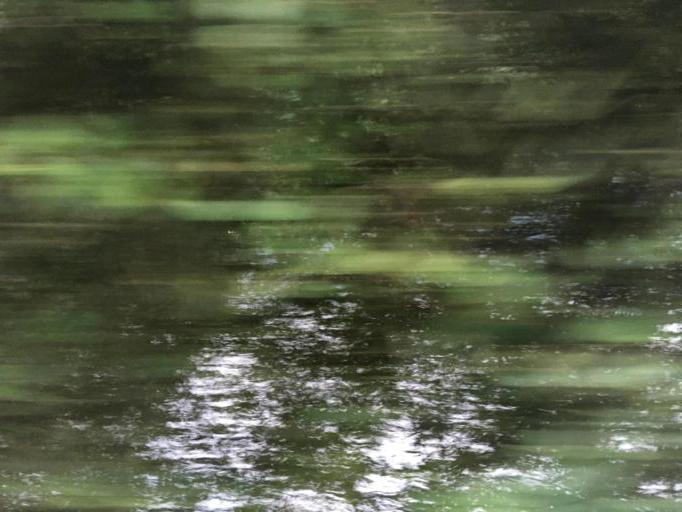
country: TW
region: Taiwan
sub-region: Chiayi
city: Jiayi Shi
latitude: 23.5360
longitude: 120.6286
